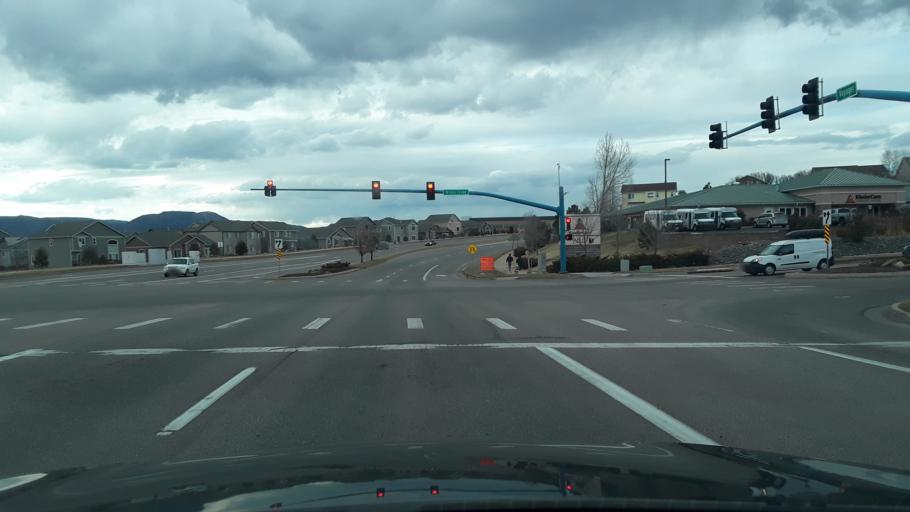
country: US
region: Colorado
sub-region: El Paso County
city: Gleneagle
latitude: 39.0104
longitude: -104.8078
